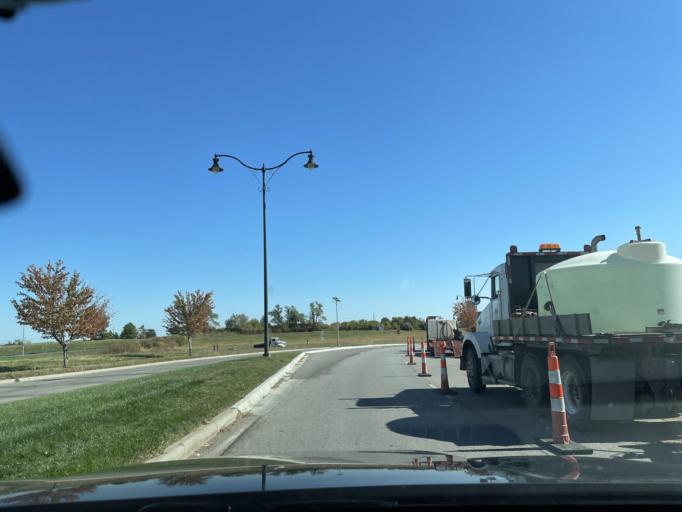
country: US
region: Missouri
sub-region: Andrew County
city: Country Club Village
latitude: 39.8161
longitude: -94.8088
